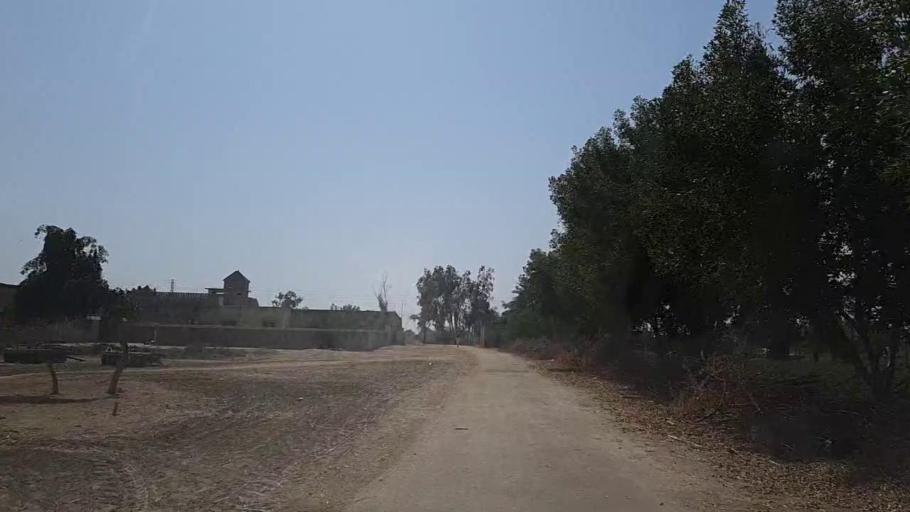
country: PK
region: Sindh
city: Samaro
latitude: 25.2370
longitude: 69.4056
